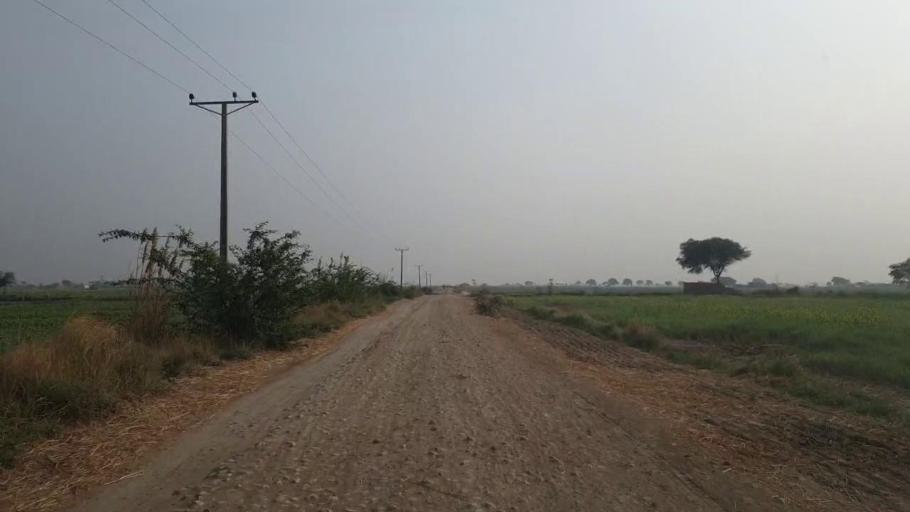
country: PK
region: Sindh
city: Mirpur Batoro
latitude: 24.5628
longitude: 68.4187
